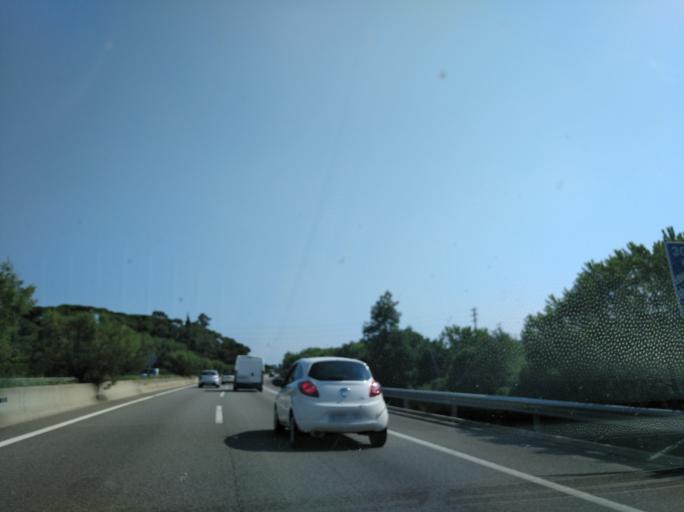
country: ES
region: Catalonia
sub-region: Provincia de Barcelona
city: Argentona
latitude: 41.5574
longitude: 2.4076
